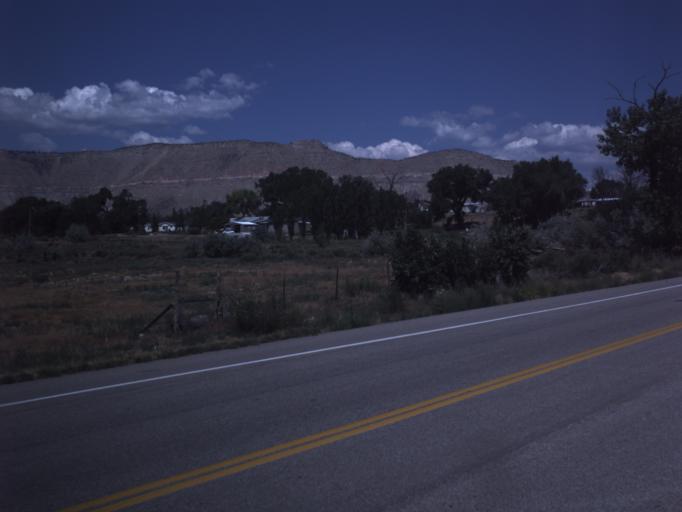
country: US
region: Utah
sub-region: Emery County
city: Ferron
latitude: 39.0958
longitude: -111.1321
